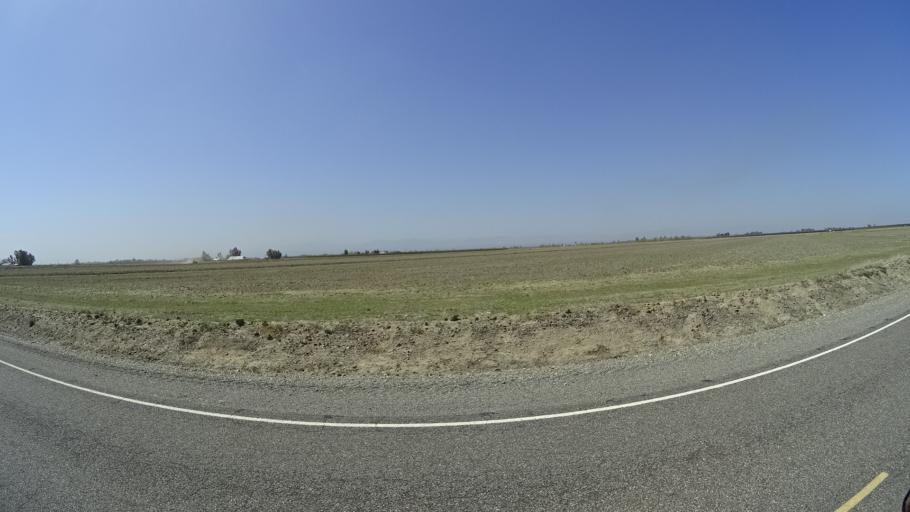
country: US
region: California
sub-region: Glenn County
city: Willows
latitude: 39.5594
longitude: -122.1370
